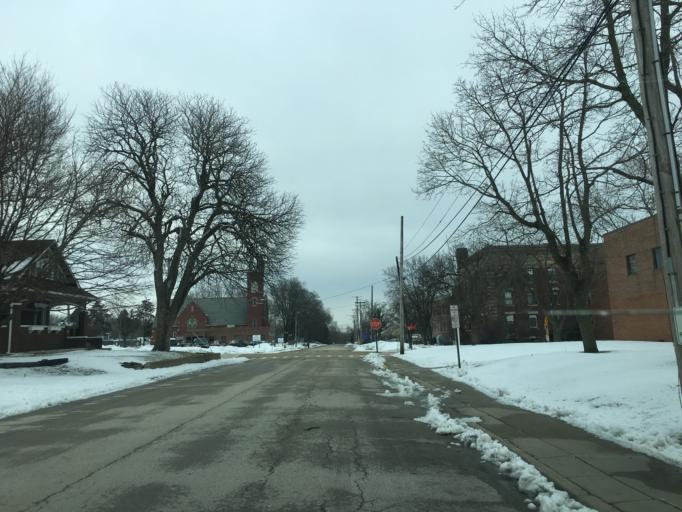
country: US
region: Illinois
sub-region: LaSalle County
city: Peru
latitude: 41.3294
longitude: -89.1259
